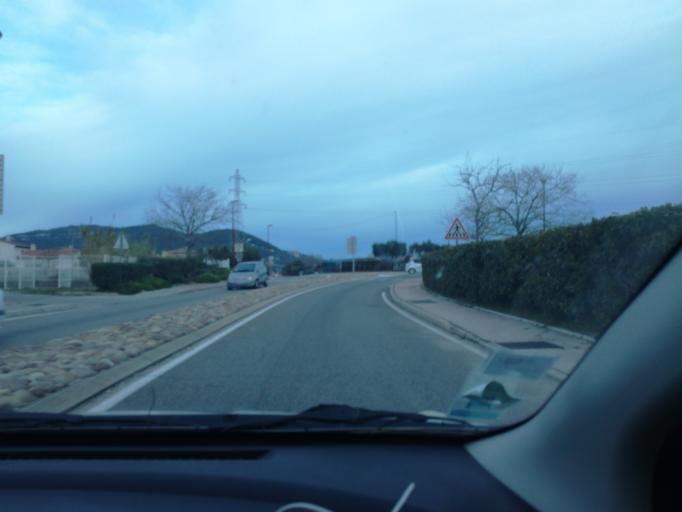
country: FR
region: Provence-Alpes-Cote d'Azur
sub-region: Departement du Var
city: La Crau
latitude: 43.1543
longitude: 6.0703
